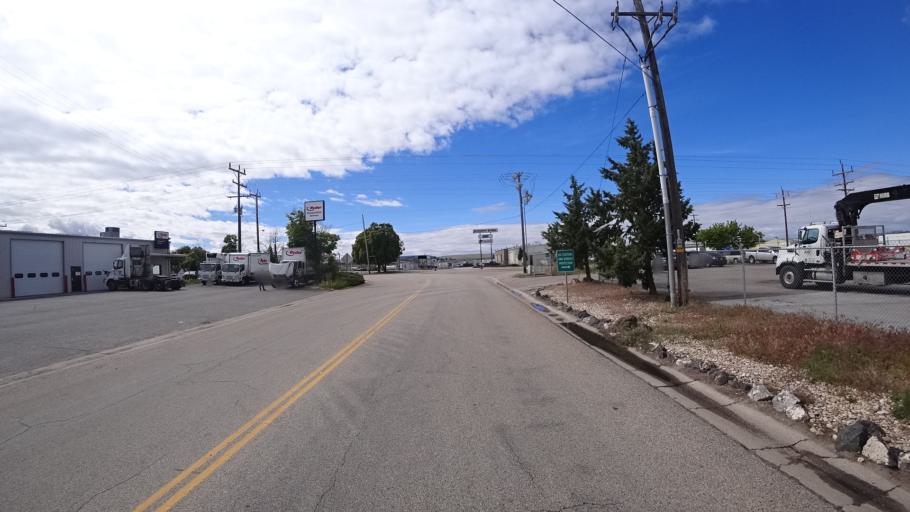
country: US
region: Idaho
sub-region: Ada County
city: Boise
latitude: 43.5610
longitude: -116.1987
